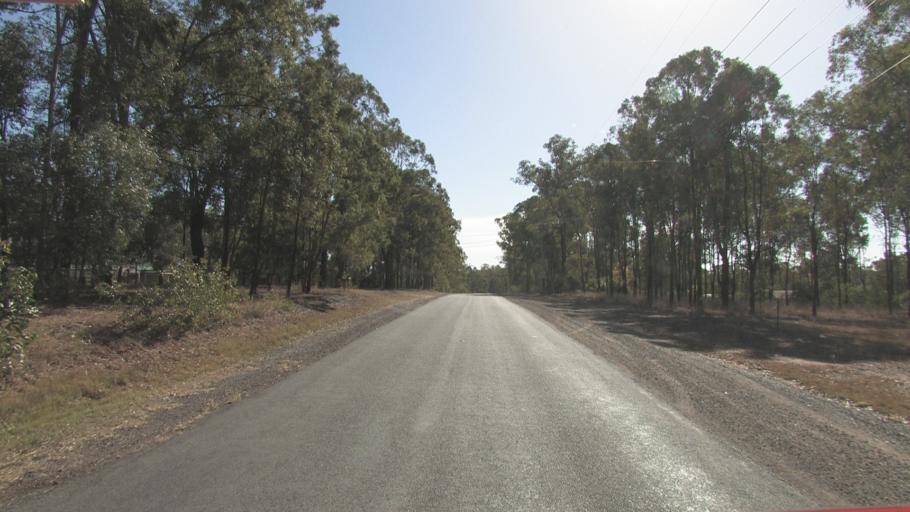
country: AU
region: Queensland
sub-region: Logan
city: Cedar Vale
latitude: -27.8602
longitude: 152.9906
